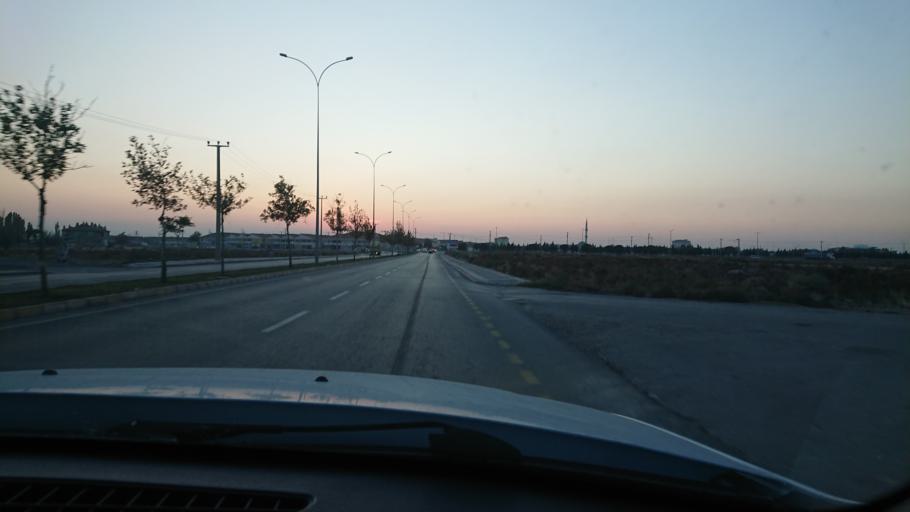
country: TR
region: Aksaray
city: Aksaray
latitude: 38.3580
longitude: 33.9928
